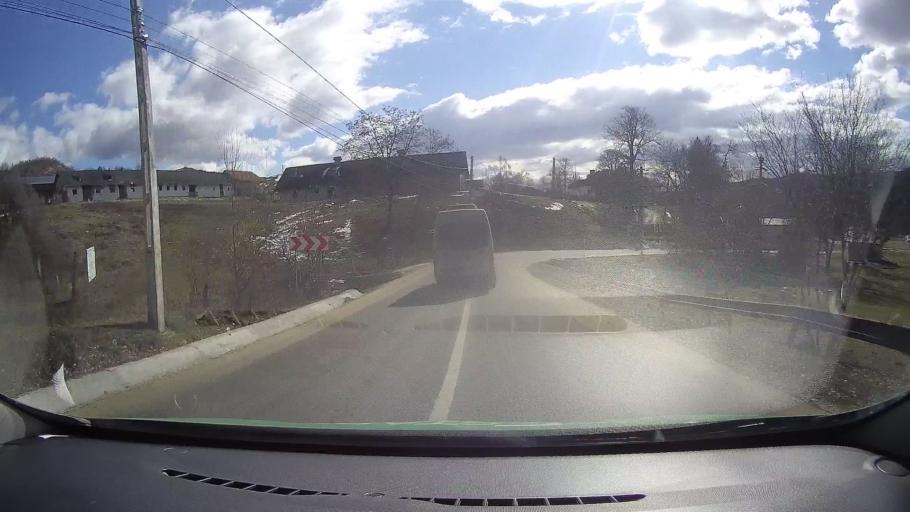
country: RO
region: Dambovita
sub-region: Comuna Runcu
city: Badeni
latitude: 45.1381
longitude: 25.4027
